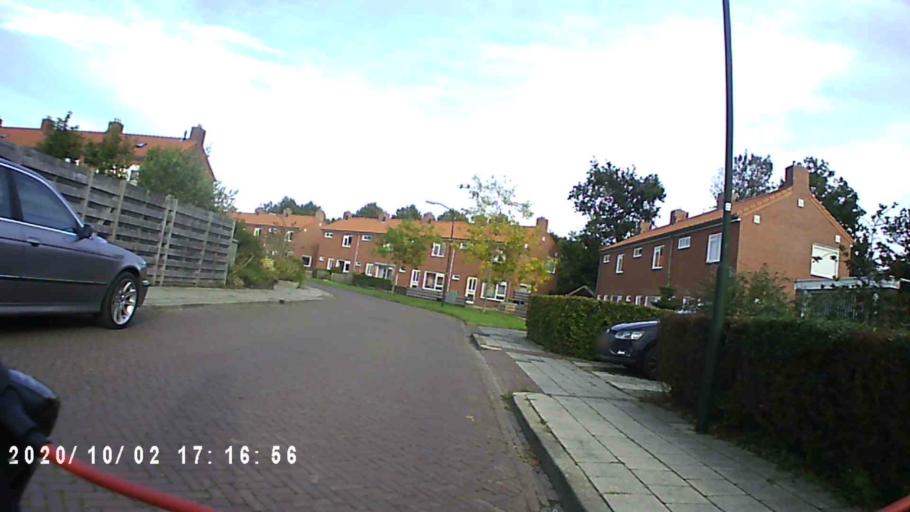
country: NL
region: Groningen
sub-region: Gemeente De Marne
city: Ulrum
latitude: 53.3385
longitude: 6.3056
